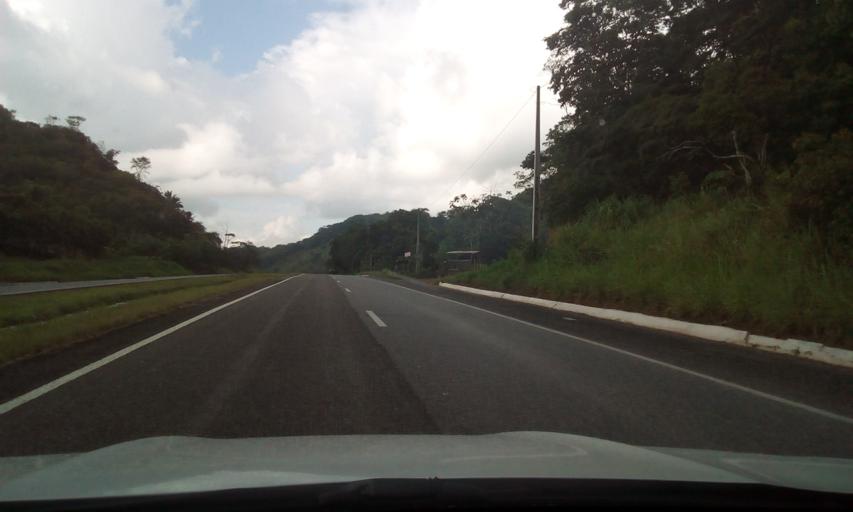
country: BR
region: Pernambuco
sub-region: Cabo De Santo Agostinho
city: Cabo
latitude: -8.2641
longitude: -35.0501
